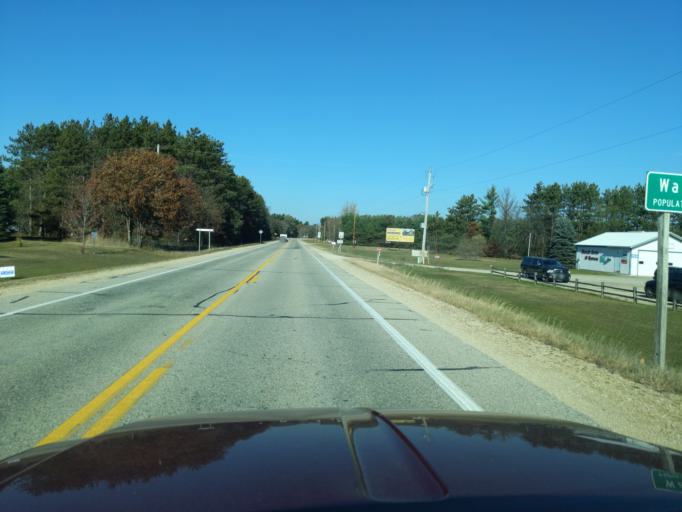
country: US
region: Wisconsin
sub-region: Waushara County
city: Wautoma
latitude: 44.0579
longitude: -89.2938
